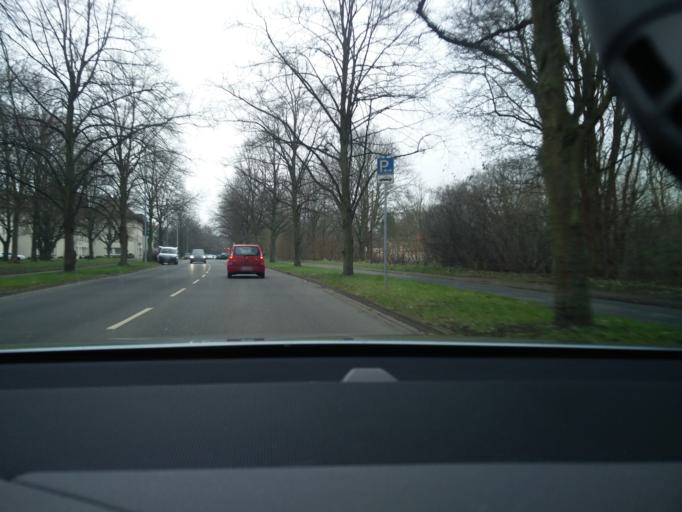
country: DE
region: Lower Saxony
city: Hannover
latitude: 52.3377
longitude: 9.7572
